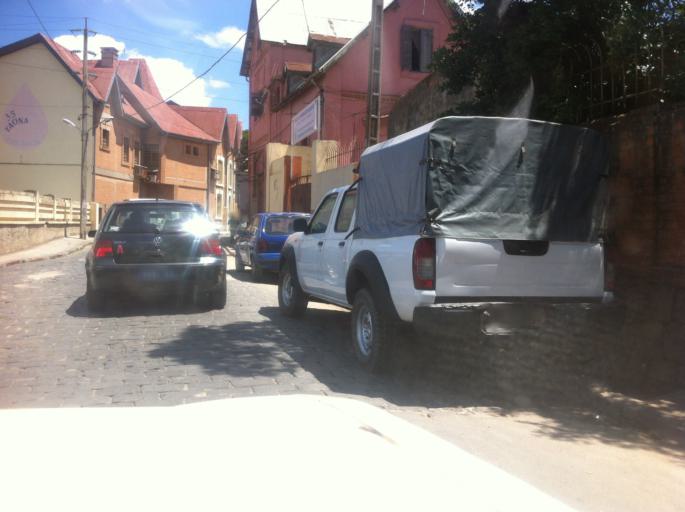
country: MG
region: Analamanga
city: Antananarivo
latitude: -18.9113
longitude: 47.5256
